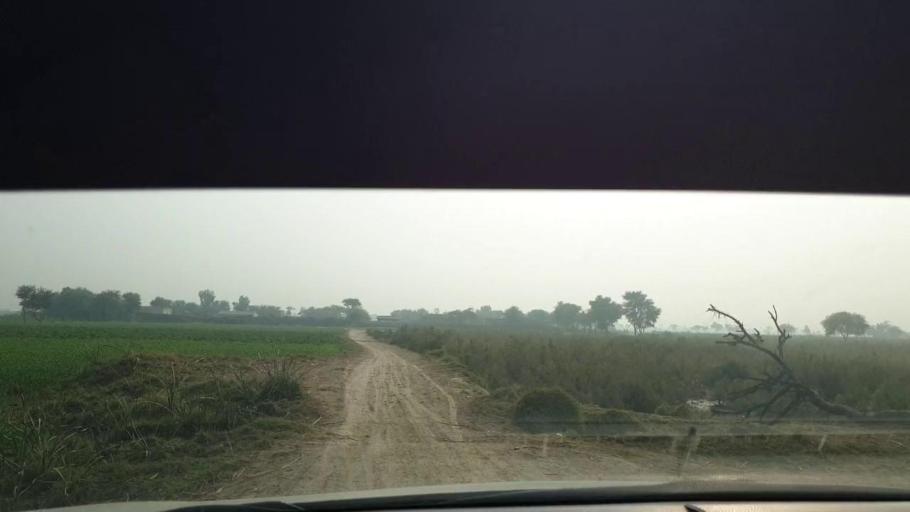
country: PK
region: Sindh
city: Berani
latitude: 25.7861
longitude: 68.8218
